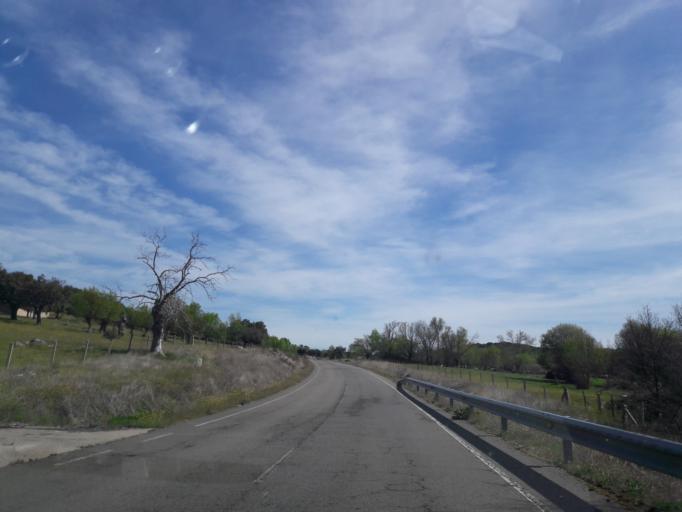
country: ES
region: Castille and Leon
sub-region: Provincia de Salamanca
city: Fuentes de Bejar
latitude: 40.4982
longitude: -5.7084
